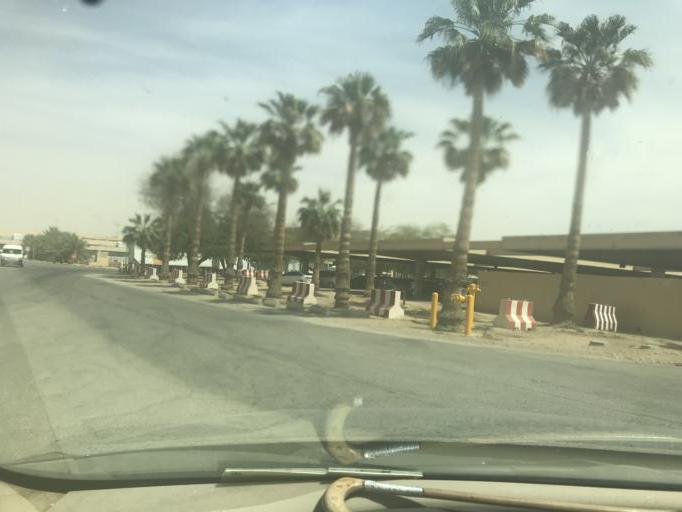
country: SA
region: Ar Riyad
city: Riyadh
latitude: 24.9744
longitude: 46.6896
